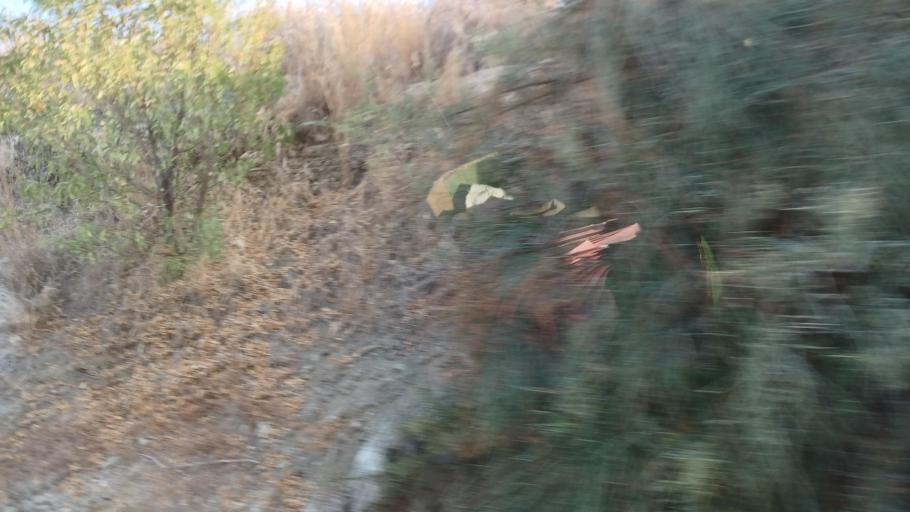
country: CY
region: Pafos
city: Polis
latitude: 35.0591
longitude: 32.4657
